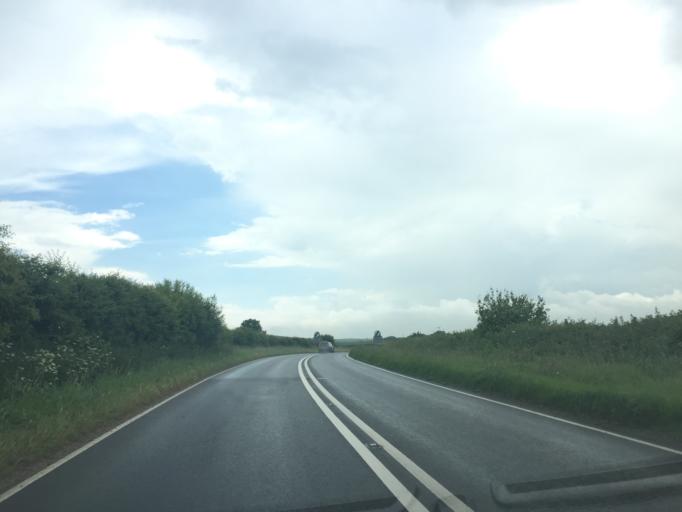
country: GB
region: England
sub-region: Dorset
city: Bovington Camp
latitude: 50.6639
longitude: -2.2879
